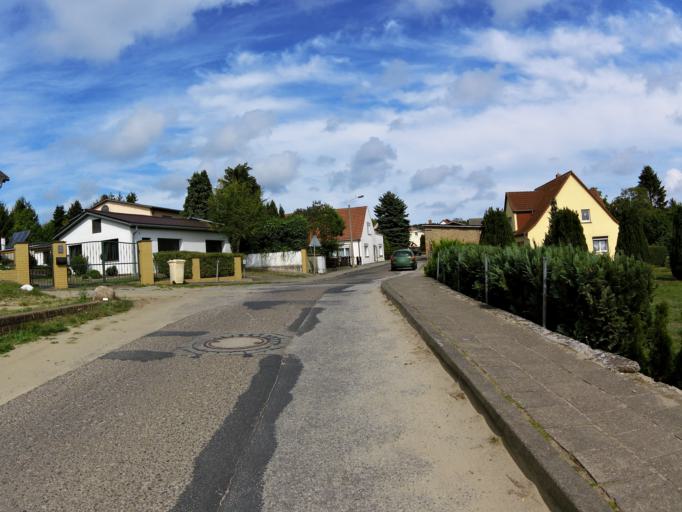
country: DE
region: Mecklenburg-Vorpommern
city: Seebad Bansin
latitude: 53.9587
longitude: 14.1287
